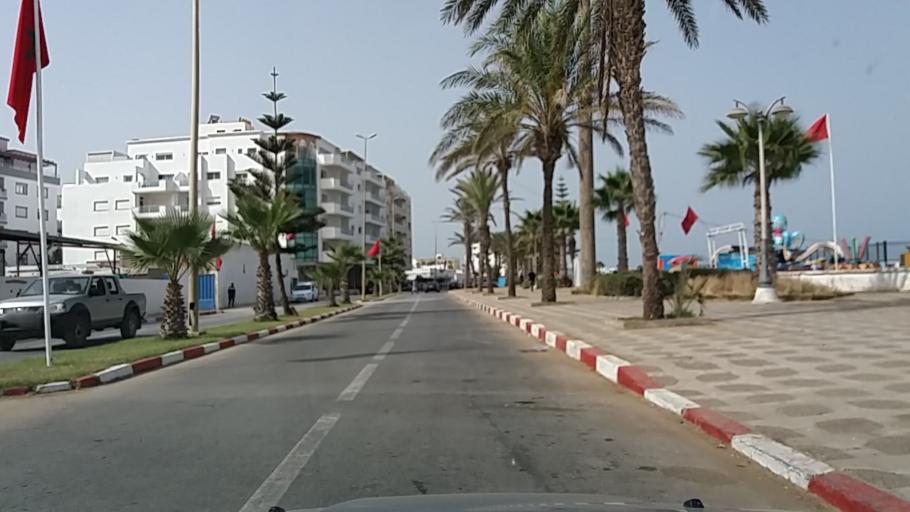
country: MA
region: Tanger-Tetouan
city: Asilah
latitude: 35.4722
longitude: -6.0295
